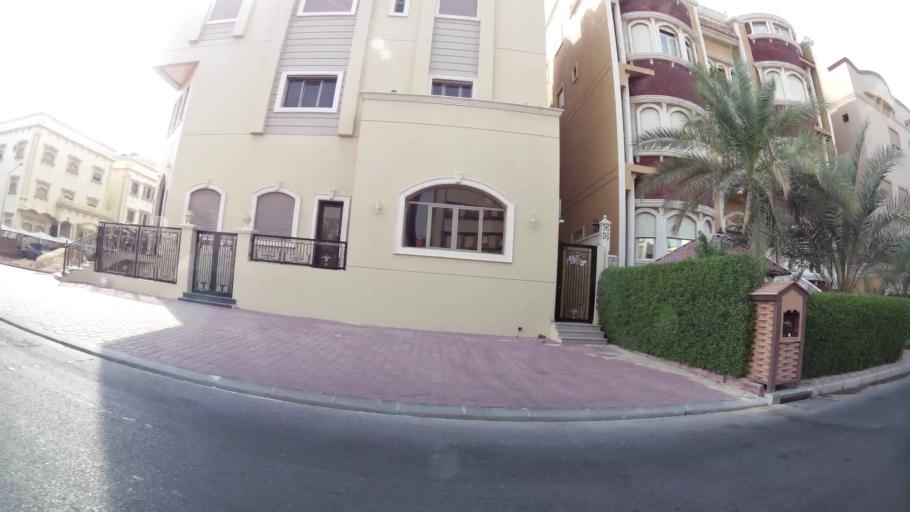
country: KW
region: Al Farwaniyah
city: Al Farwaniyah
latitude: 29.2725
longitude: 47.9394
